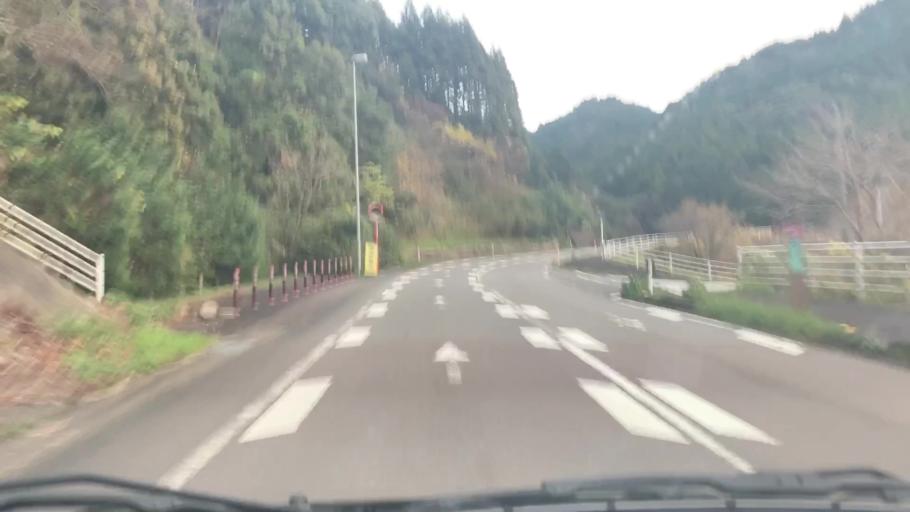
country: JP
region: Saga Prefecture
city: Kashima
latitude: 33.0507
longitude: 130.0735
